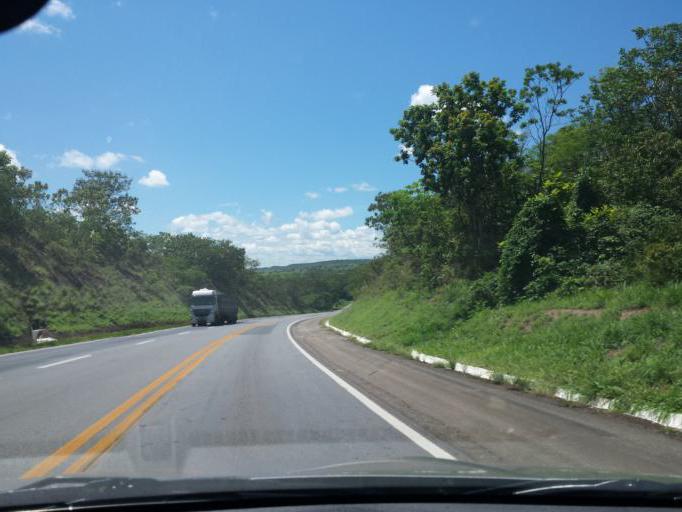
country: BR
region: Goias
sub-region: Luziania
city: Luziania
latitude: -16.3819
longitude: -47.8269
